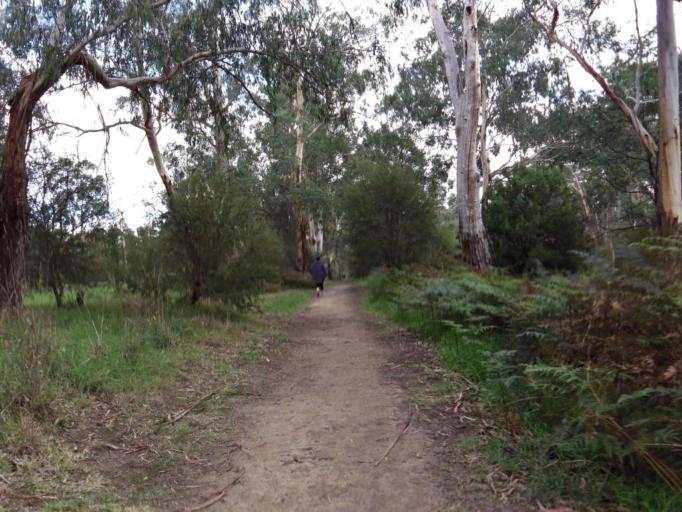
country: AU
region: Victoria
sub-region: Nillumbik
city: North Warrandyte
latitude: -37.7417
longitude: 145.2072
